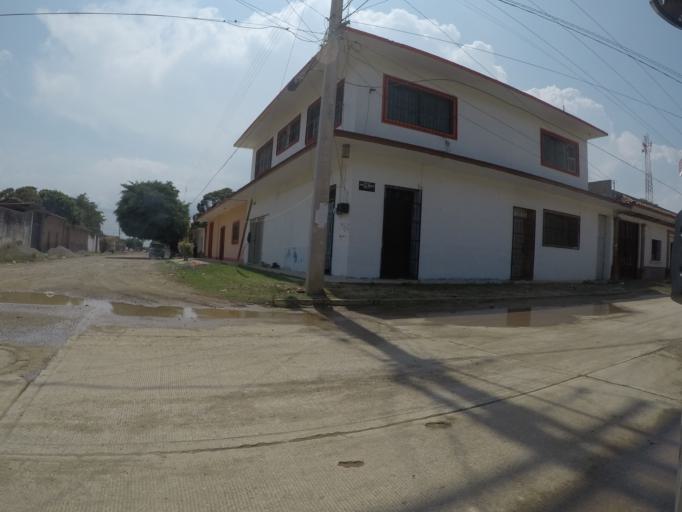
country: MX
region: Oaxaca
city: Union Hidalgo
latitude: 16.4736
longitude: -94.8317
